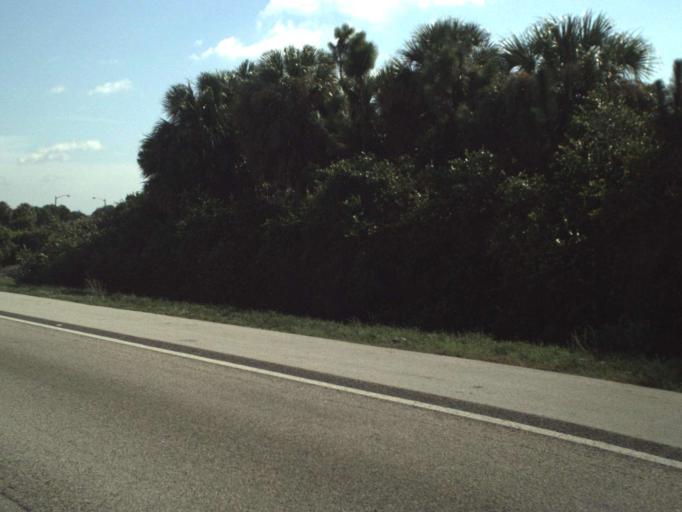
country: US
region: Florida
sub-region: Palm Beach County
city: Mangonia Park
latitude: 26.7508
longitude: -80.0899
